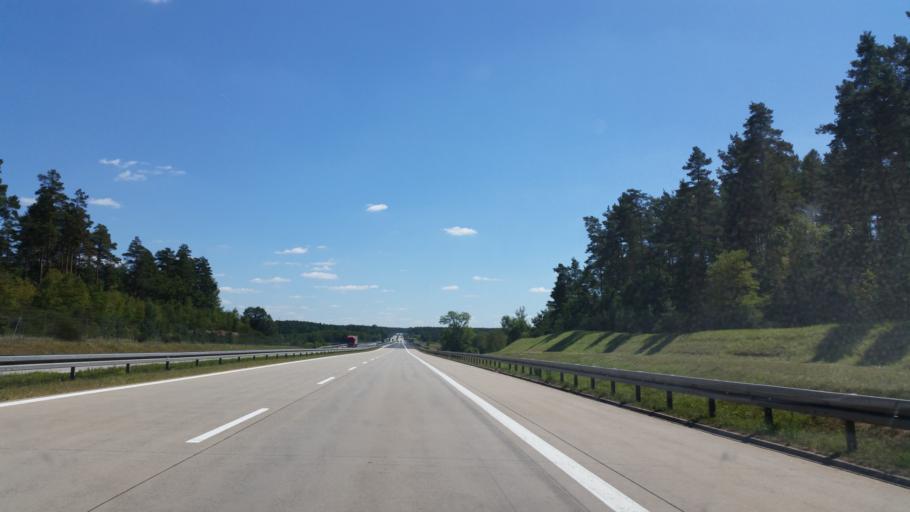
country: PL
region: Lower Silesian Voivodeship
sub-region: Powiat boleslawiecki
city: Boleslawiec
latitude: 51.3653
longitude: 15.5756
